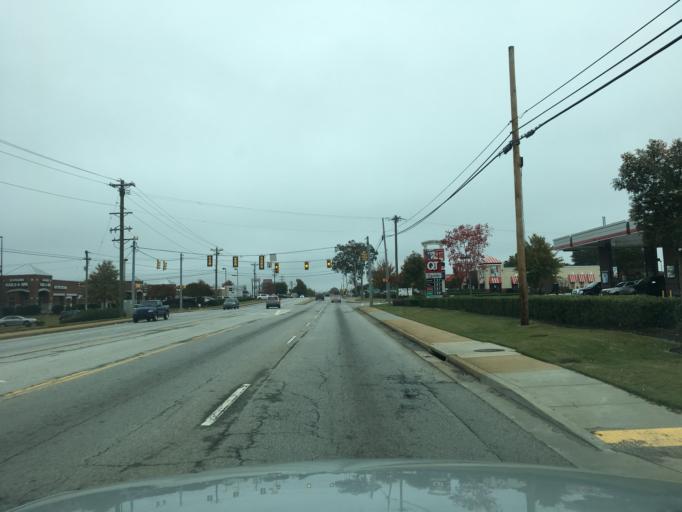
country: US
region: South Carolina
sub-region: Greenville County
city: Mauldin
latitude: 34.8210
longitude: -82.2821
